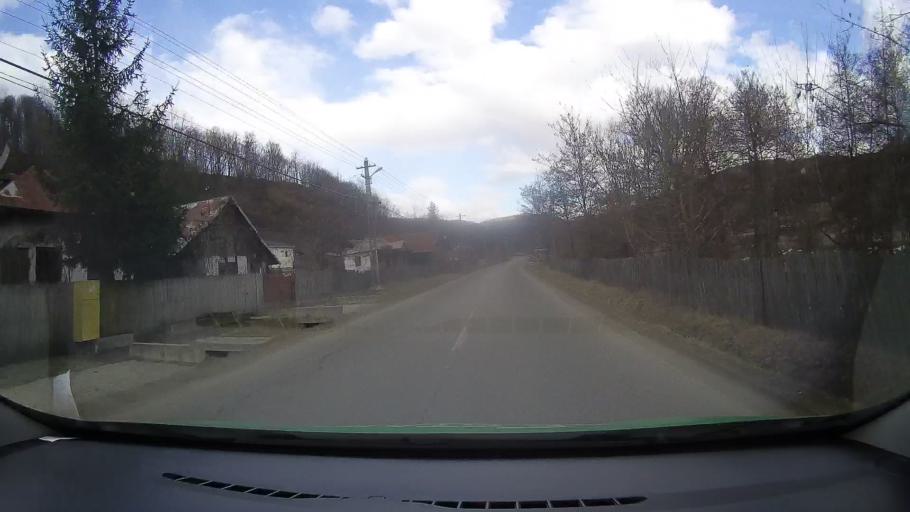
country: RO
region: Dambovita
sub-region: Comuna Visinesti
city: Visinesti
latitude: 45.0685
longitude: 25.5464
